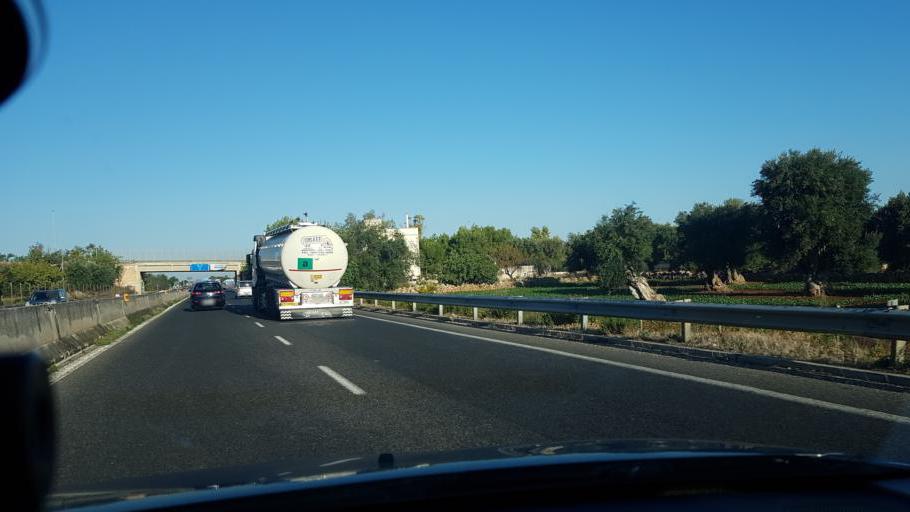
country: IT
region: Apulia
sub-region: Provincia di Bari
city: Monopoli
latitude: 40.9346
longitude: 17.2944
